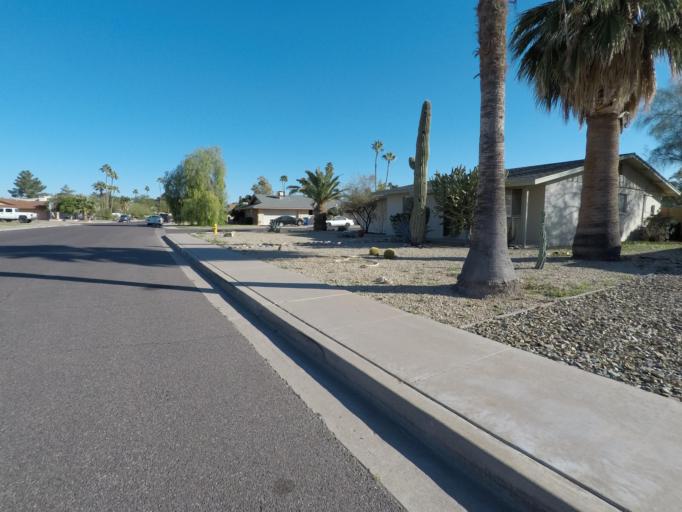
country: US
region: Arizona
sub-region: Maricopa County
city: Guadalupe
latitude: 33.3829
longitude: -111.9321
